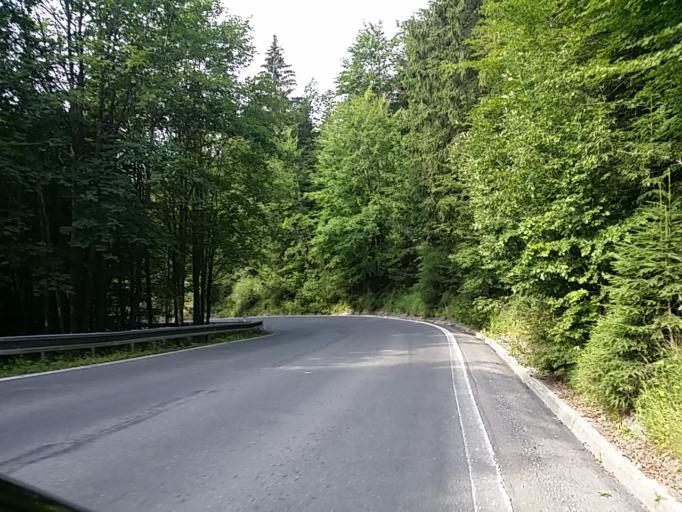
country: SK
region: Kosicky
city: Dobsina
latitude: 48.8948
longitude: 20.2479
